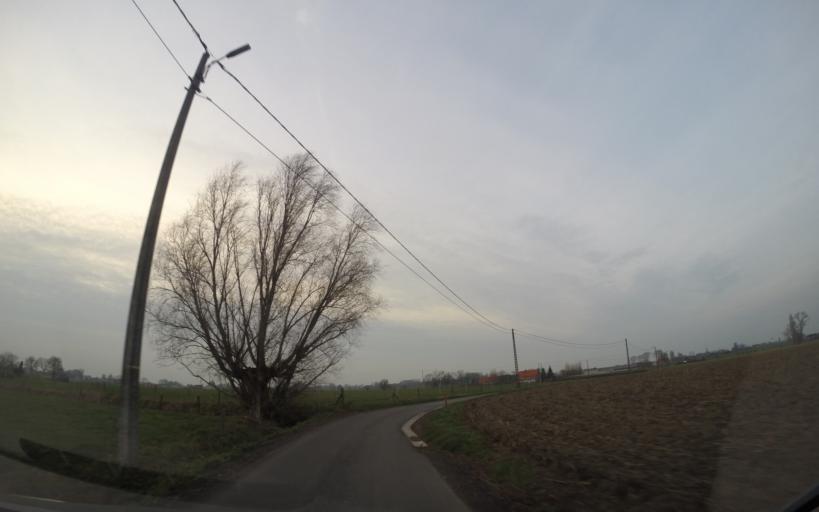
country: BE
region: Flanders
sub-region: Provincie West-Vlaanderen
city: Ruiselede
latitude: 51.0078
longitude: 3.4239
